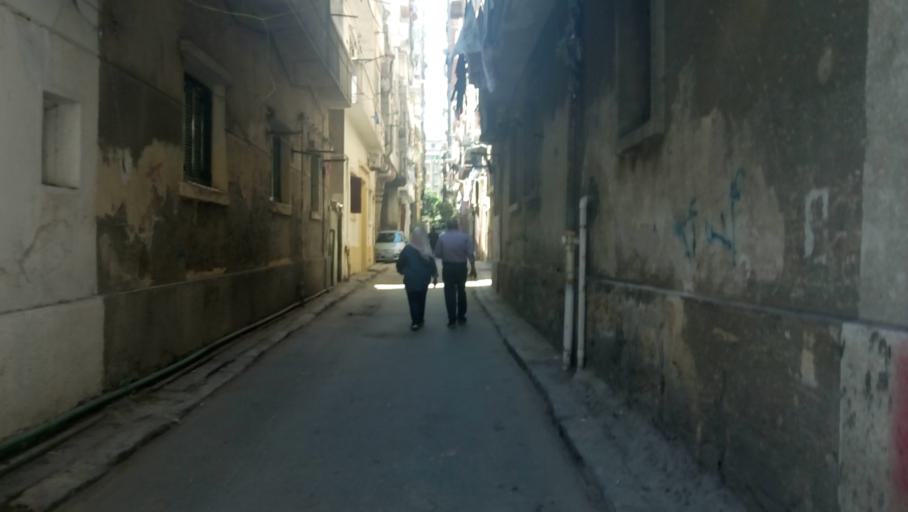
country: EG
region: Alexandria
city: Alexandria
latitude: 31.2186
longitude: 29.9371
